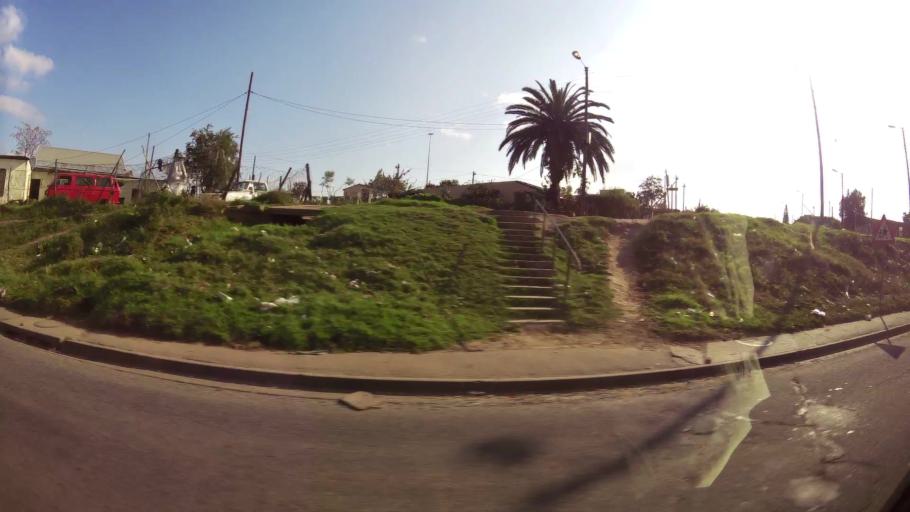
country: ZA
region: Eastern Cape
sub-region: Nelson Mandela Bay Metropolitan Municipality
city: Uitenhage
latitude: -33.7560
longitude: 25.3879
